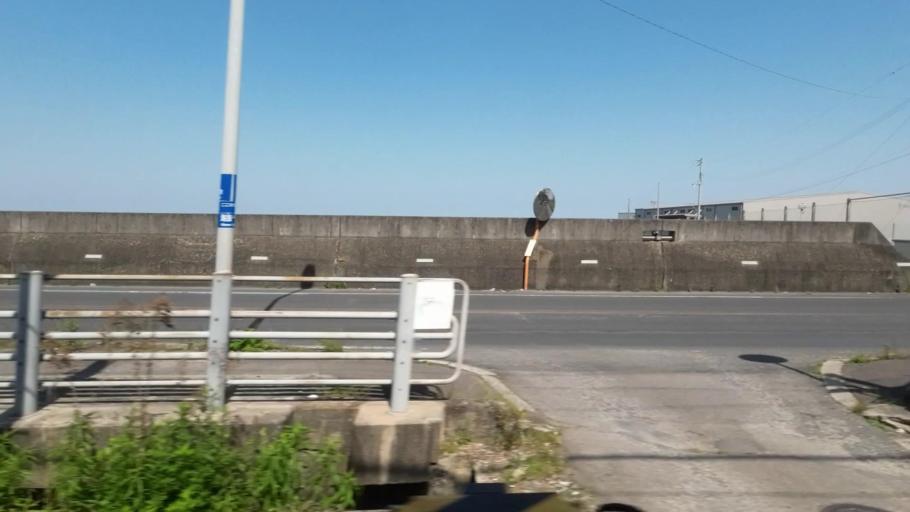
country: JP
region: Ehime
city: Kawanoecho
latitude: 34.0238
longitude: 133.5803
